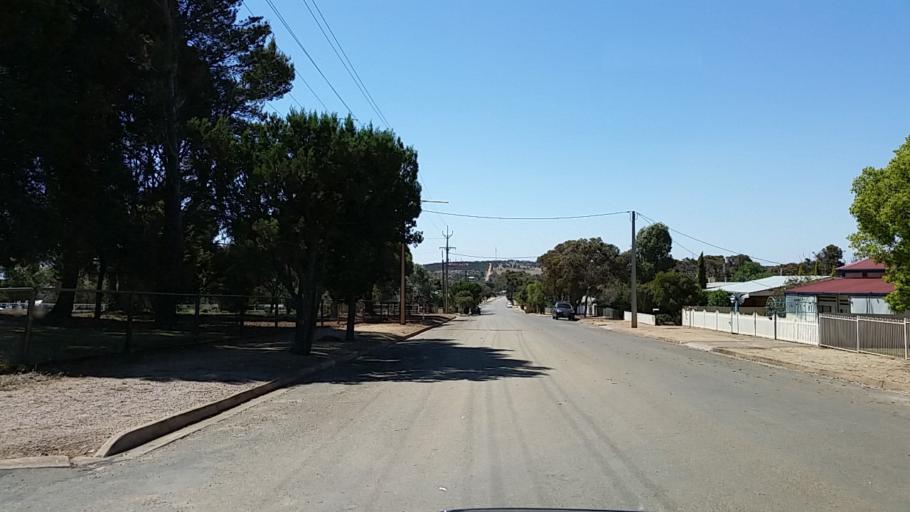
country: AU
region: South Australia
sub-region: Peterborough
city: Peterborough
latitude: -32.9806
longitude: 138.8318
